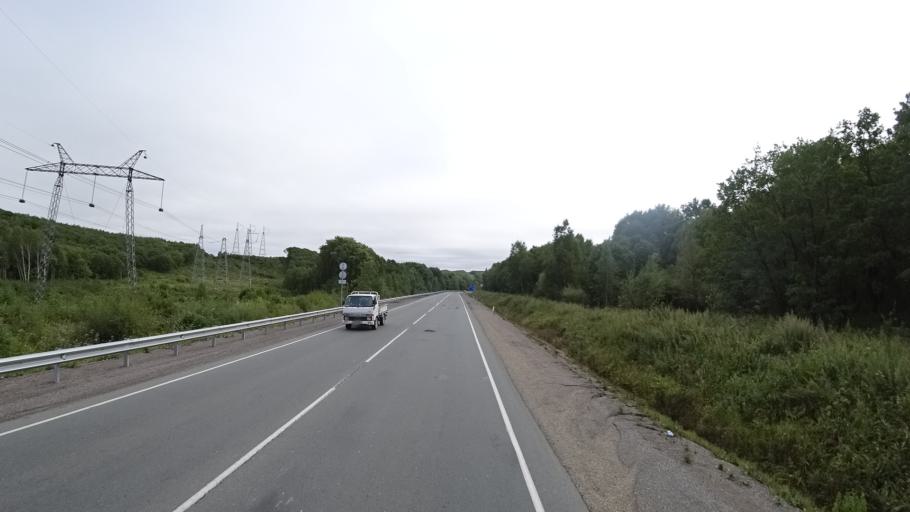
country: RU
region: Primorskiy
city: Lyalichi
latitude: 44.1061
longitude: 132.4218
